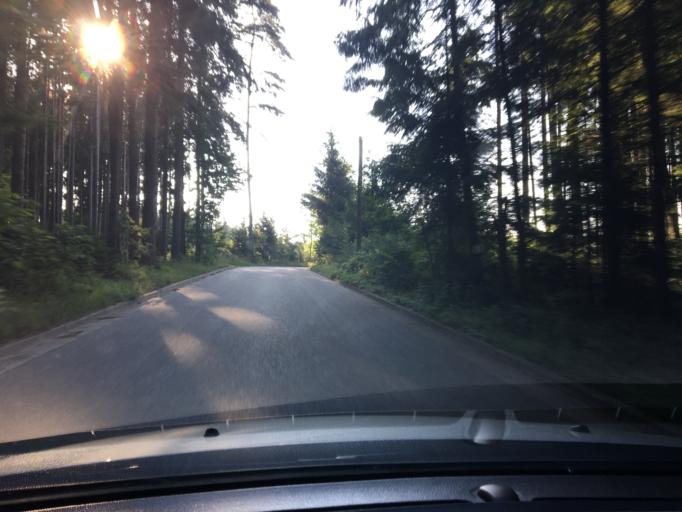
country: DE
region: Bavaria
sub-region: Lower Bavaria
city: Geisenhausen
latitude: 48.4492
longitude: 12.2999
